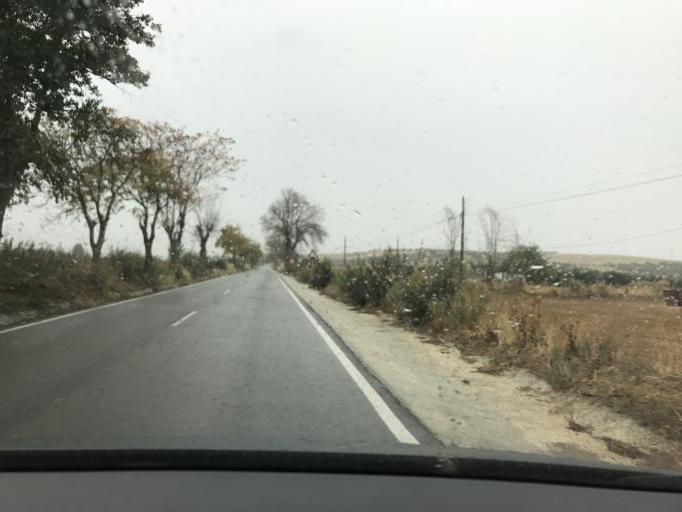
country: ES
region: Andalusia
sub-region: Provincia de Granada
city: Escuzar
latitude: 37.0938
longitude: -3.7340
